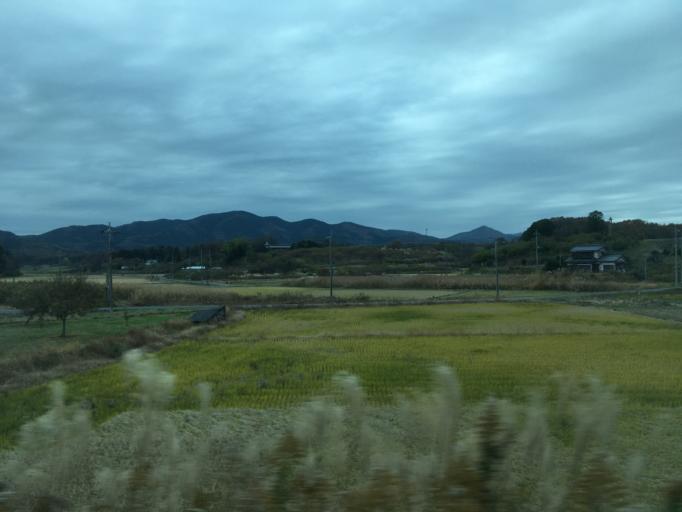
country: JP
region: Ibaraki
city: Tomobe
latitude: 36.3527
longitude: 140.2764
